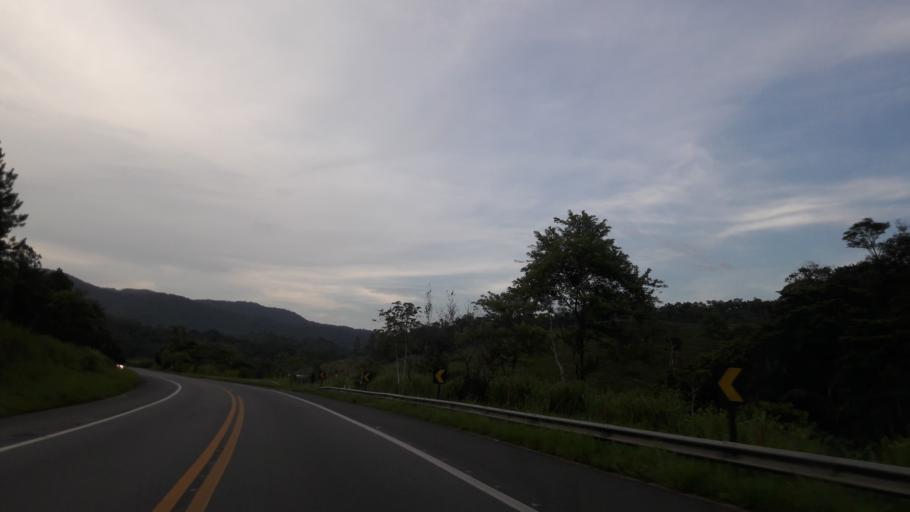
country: BR
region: Sao Paulo
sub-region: Miracatu
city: Miracatu
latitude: -24.2724
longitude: -47.2621
